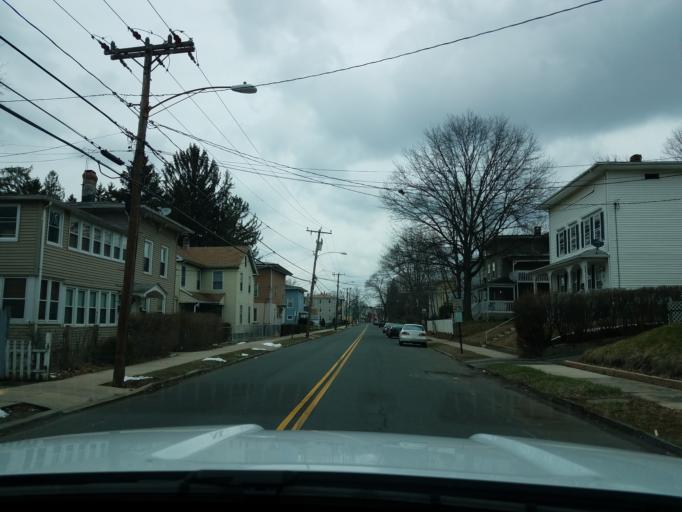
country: US
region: Connecticut
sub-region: Hartford County
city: New Britain
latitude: 41.6576
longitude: -72.7815
